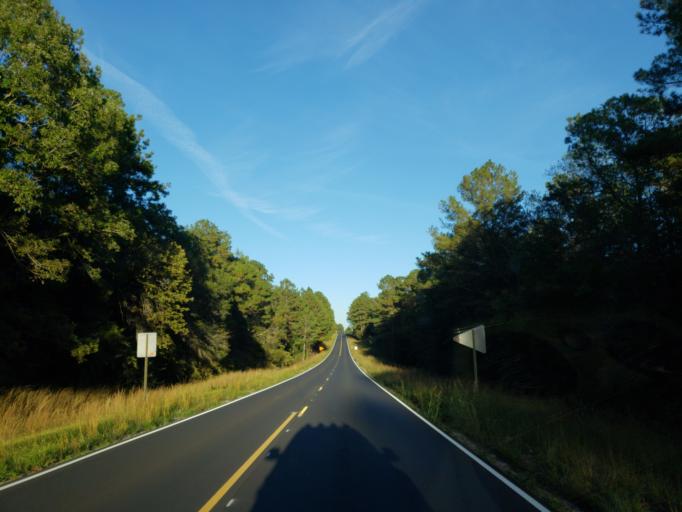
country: US
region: Mississippi
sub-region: Wayne County
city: Belmont
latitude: 31.4159
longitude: -88.5858
